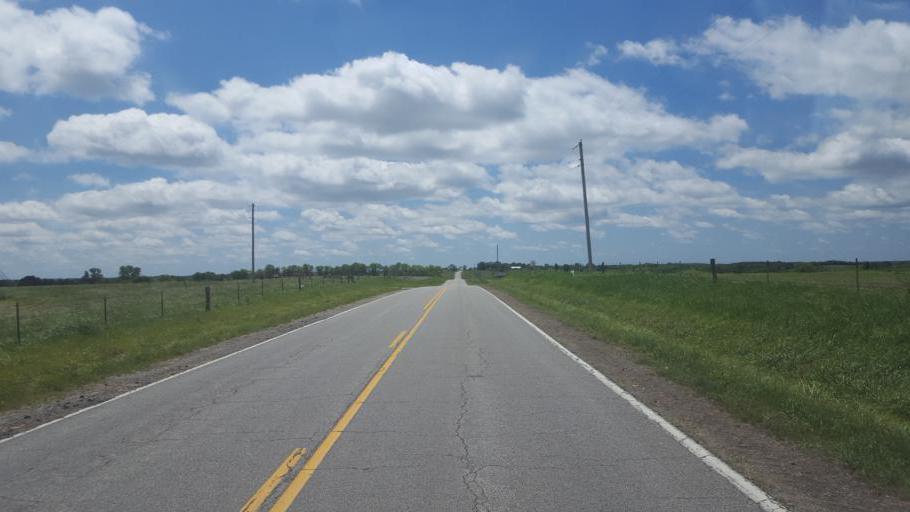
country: US
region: Missouri
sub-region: Harrison County
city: Bethany
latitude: 40.3644
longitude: -94.0110
